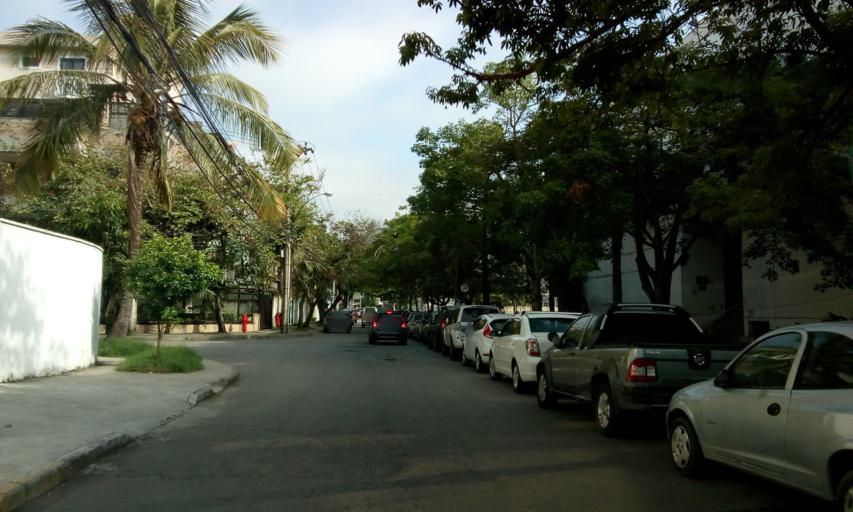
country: BR
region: Rio de Janeiro
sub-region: Nilopolis
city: Nilopolis
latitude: -23.0106
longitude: -43.4434
